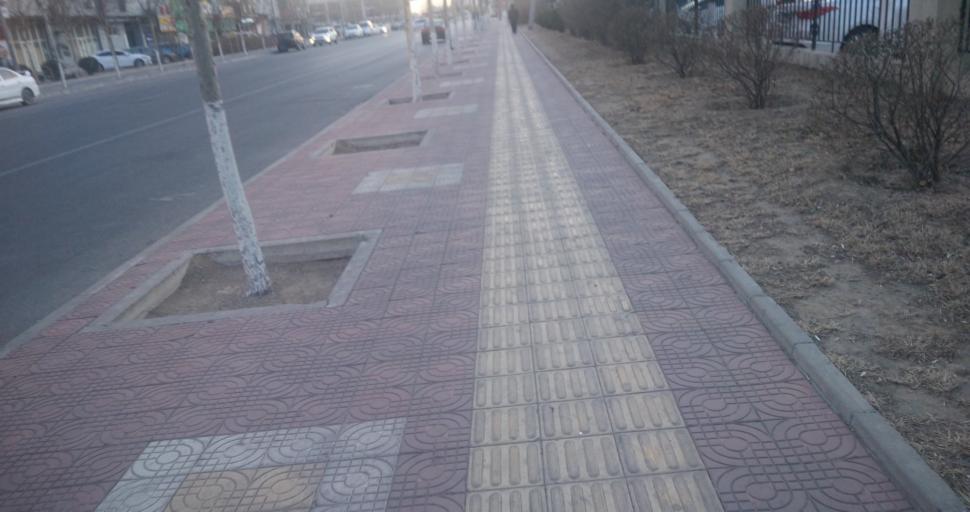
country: CN
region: Beijing
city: Yinghai
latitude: 39.7581
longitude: 116.4960
